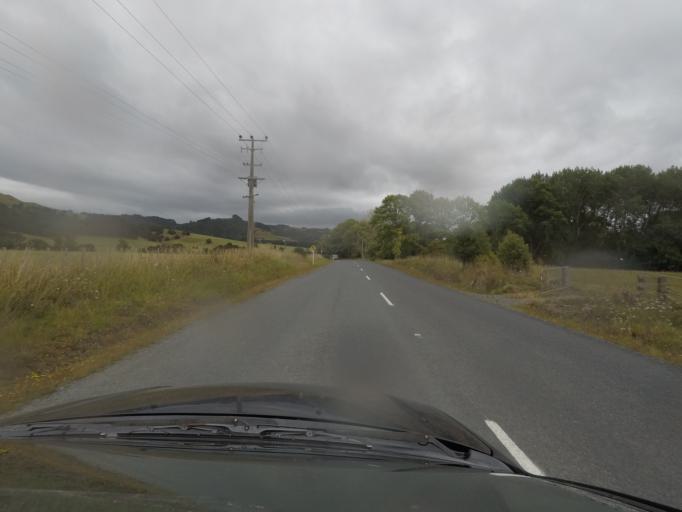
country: NZ
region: Auckland
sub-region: Auckland
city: Warkworth
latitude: -36.2865
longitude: 174.6624
